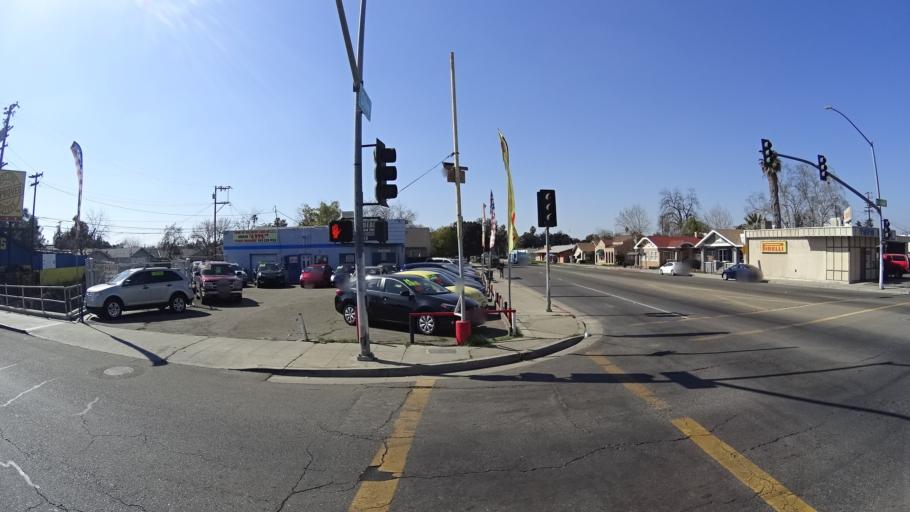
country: US
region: California
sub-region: Fresno County
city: Fresno
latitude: 36.7577
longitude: -119.7906
